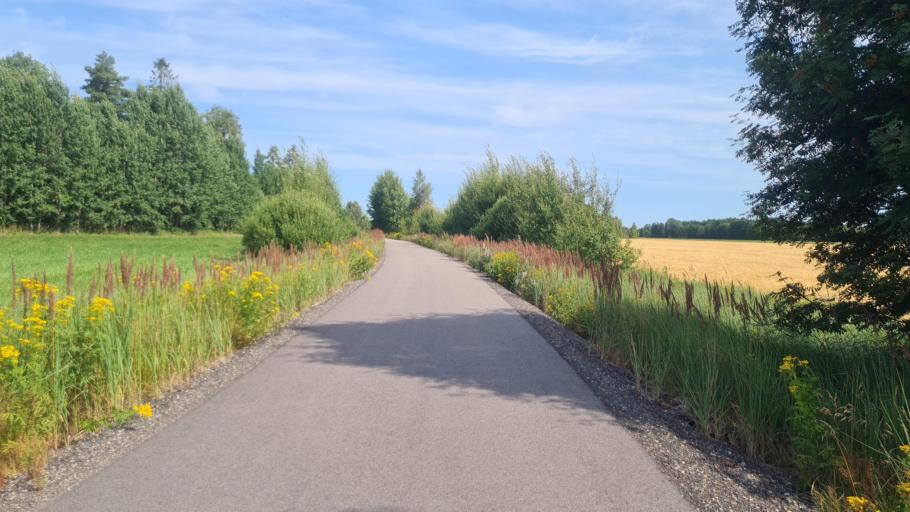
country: SE
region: Kronoberg
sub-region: Ljungby Kommun
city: Lagan
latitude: 56.8975
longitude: 13.9884
